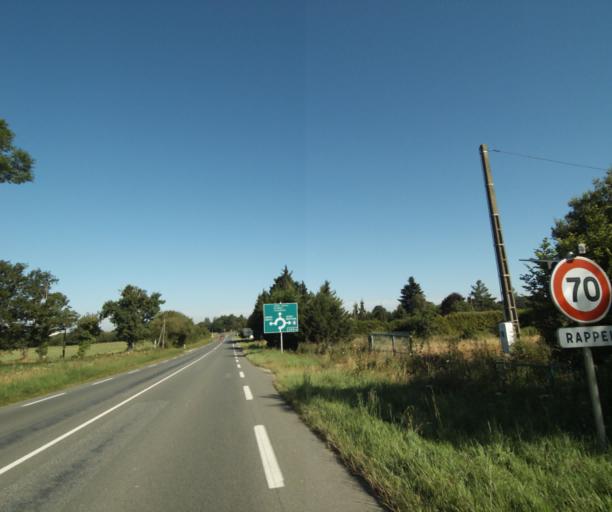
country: FR
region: Pays de la Loire
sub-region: Departement de la Mayenne
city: Bonchamp-les-Laval
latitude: 48.0475
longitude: -0.7306
